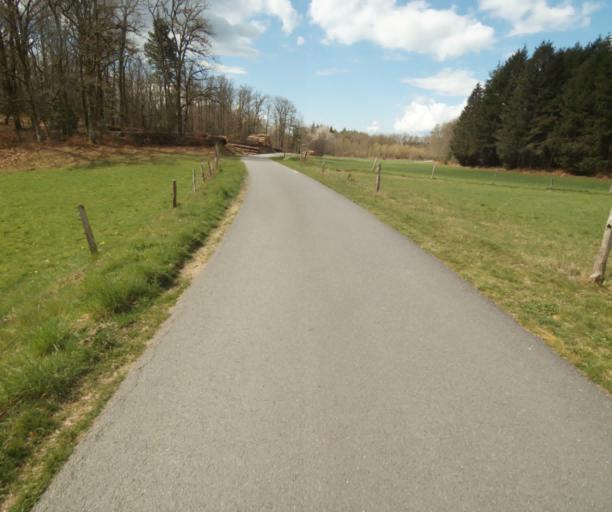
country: FR
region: Limousin
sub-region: Departement de la Correze
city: Correze
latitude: 45.2778
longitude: 1.9044
